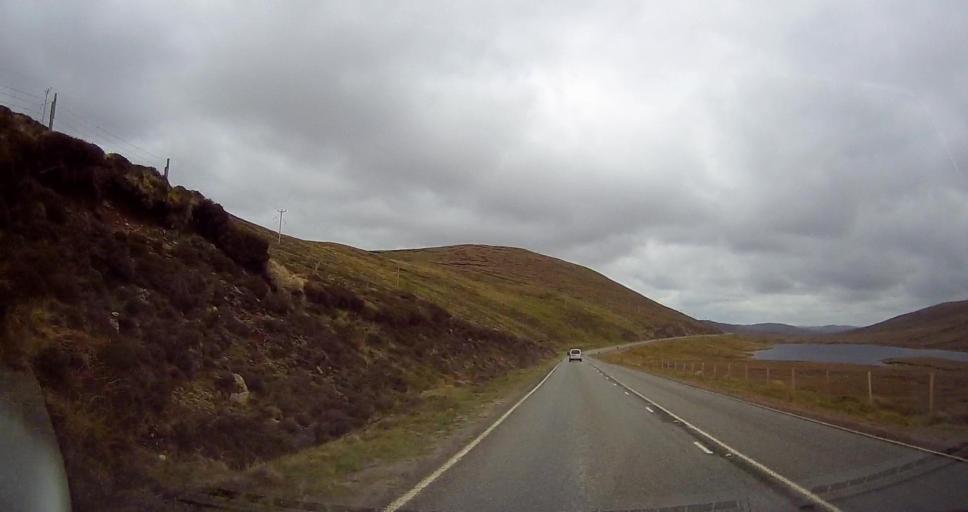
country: GB
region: Scotland
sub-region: Shetland Islands
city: Lerwick
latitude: 60.3204
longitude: -1.2492
